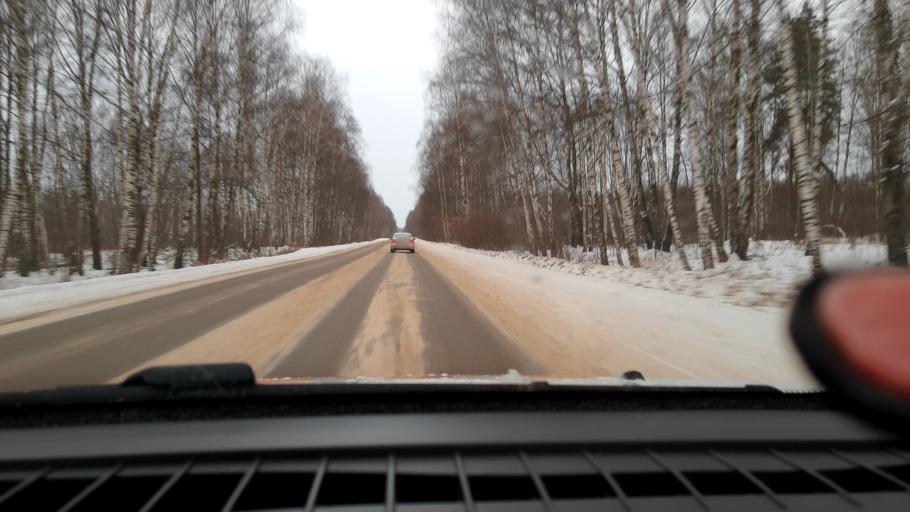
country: RU
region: Nizjnij Novgorod
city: Afonino
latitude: 56.3177
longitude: 44.1966
